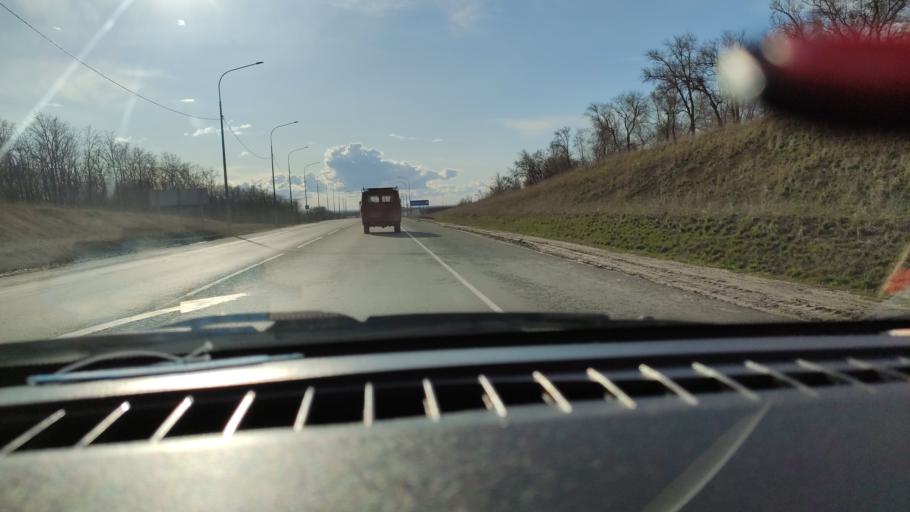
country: RU
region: Saratov
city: Yelshanka
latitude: 51.8248
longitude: 46.2975
